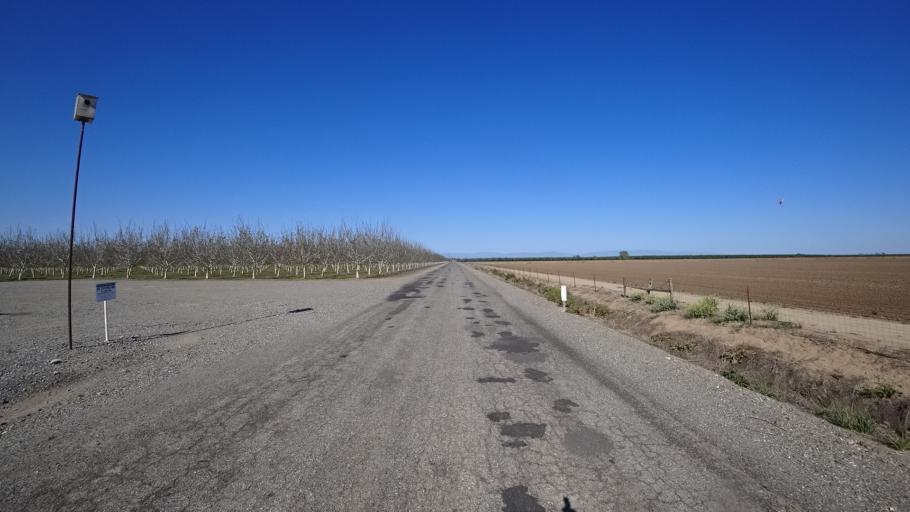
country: US
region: California
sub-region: Glenn County
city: Hamilton City
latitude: 39.6782
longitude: -122.0457
